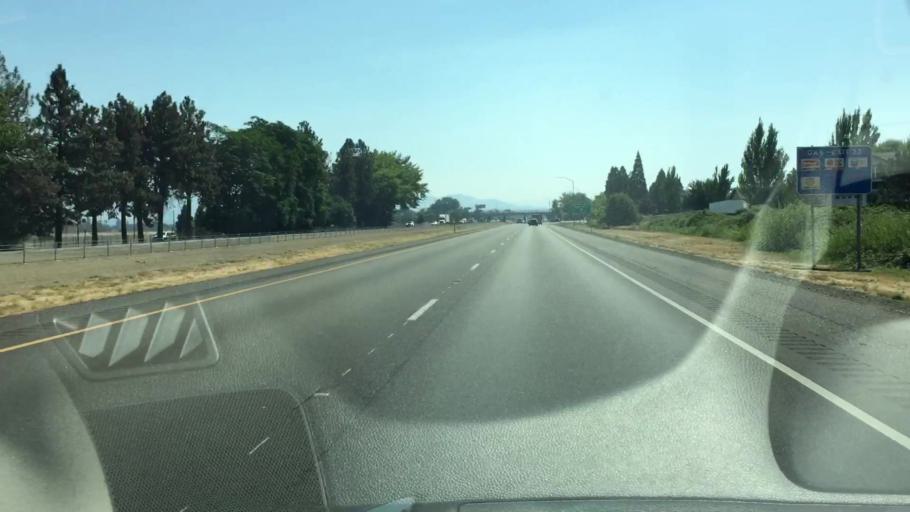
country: US
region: Oregon
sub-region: Jackson County
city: Central Point
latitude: 42.3836
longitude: -122.9113
